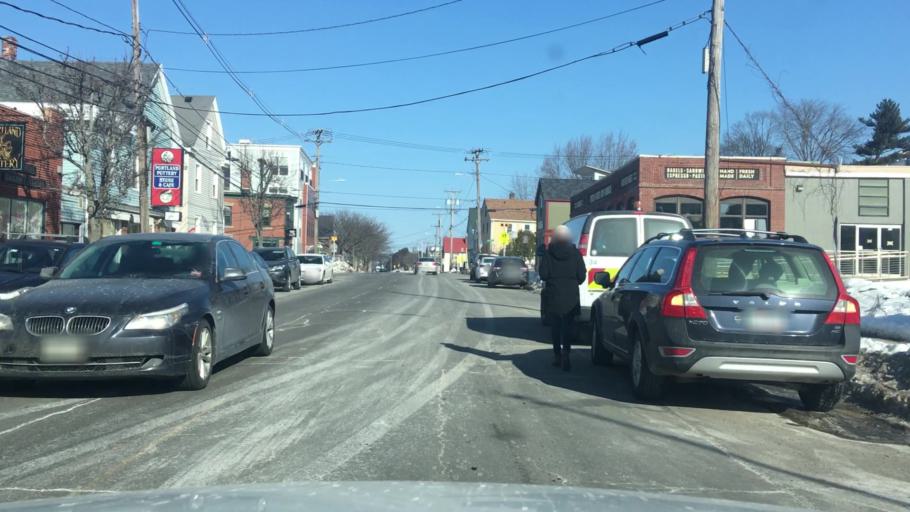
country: US
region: Maine
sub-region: Cumberland County
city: Portland
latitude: 43.6671
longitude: -70.2530
